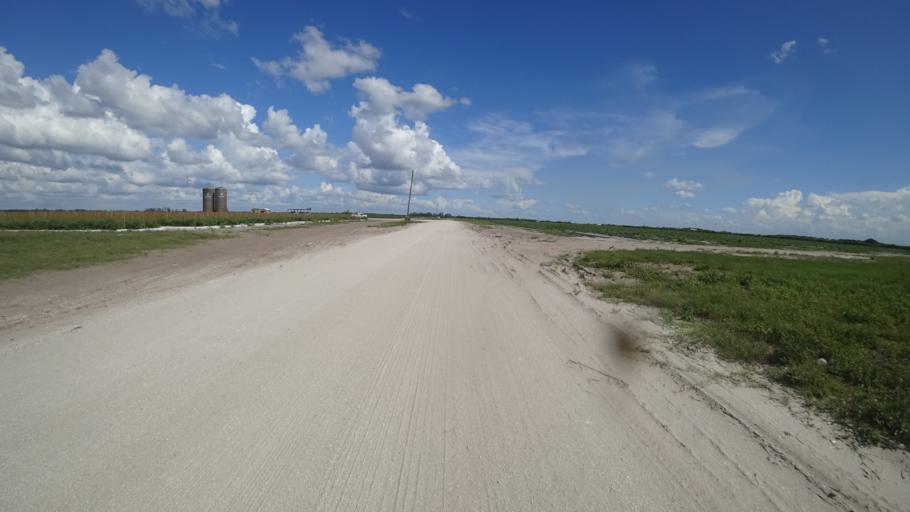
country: US
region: Florida
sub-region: DeSoto County
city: Arcadia
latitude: 27.3244
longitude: -82.0982
